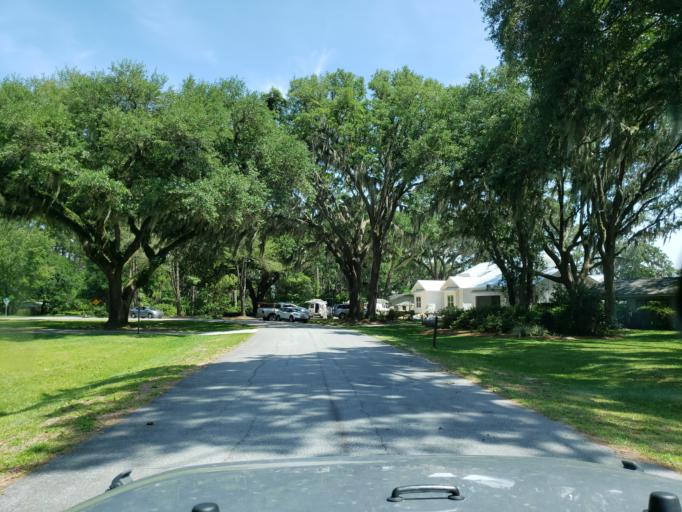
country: US
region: Georgia
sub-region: Chatham County
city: Whitemarsh Island
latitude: 32.0256
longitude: -81.0039
